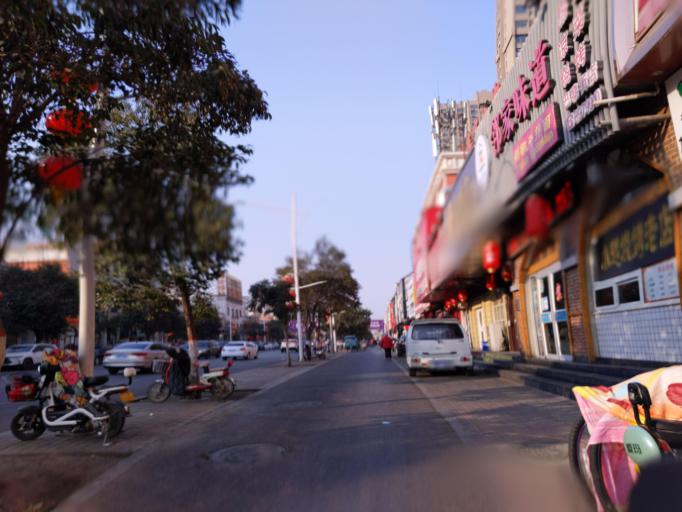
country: CN
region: Henan Sheng
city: Puyang
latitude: 35.7751
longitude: 115.0329
